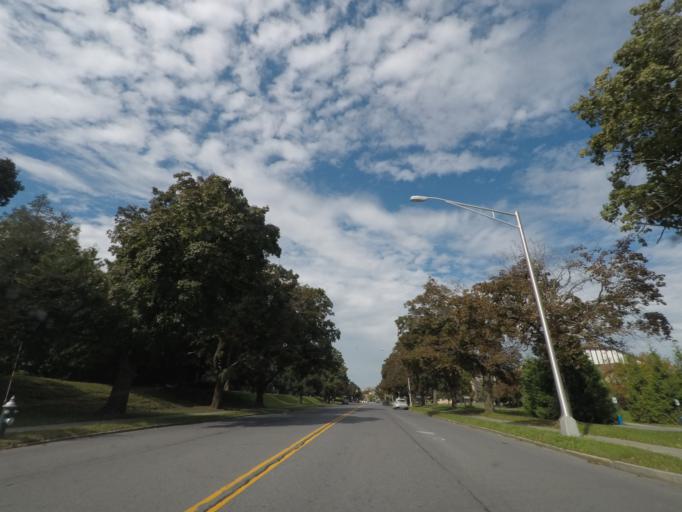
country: US
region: New York
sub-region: Albany County
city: Albany
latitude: 42.6485
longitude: -73.7736
